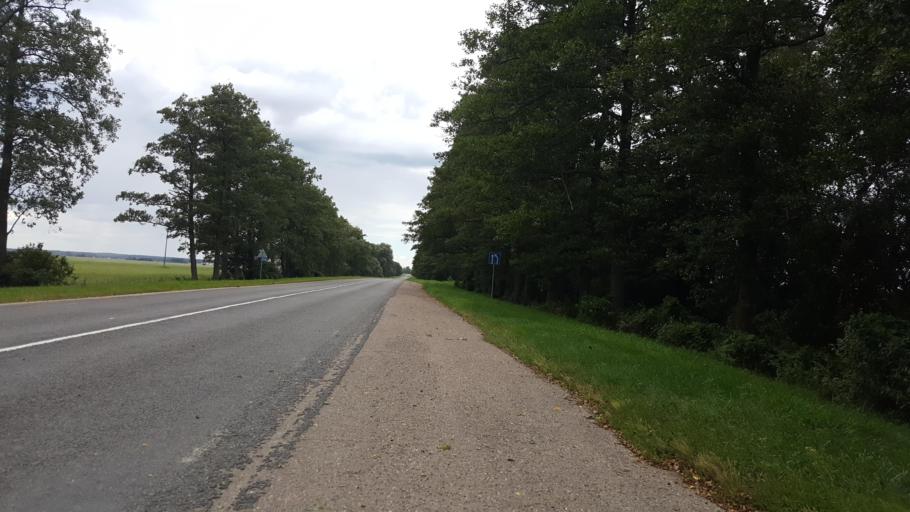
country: BY
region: Brest
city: Zhabinka
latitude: 52.2996
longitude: 23.9346
